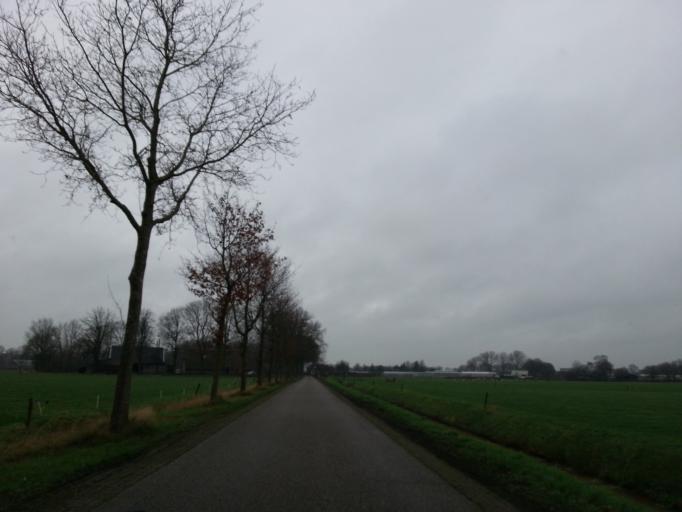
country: NL
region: Overijssel
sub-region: Gemeente Dalfsen
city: Dalfsen
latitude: 52.5130
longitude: 6.2362
